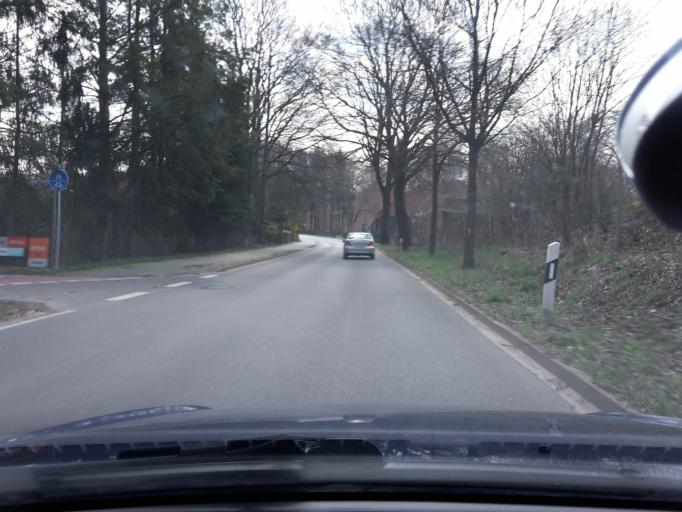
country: DE
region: Lower Saxony
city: Jesteburg
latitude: 53.2911
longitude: 9.9129
